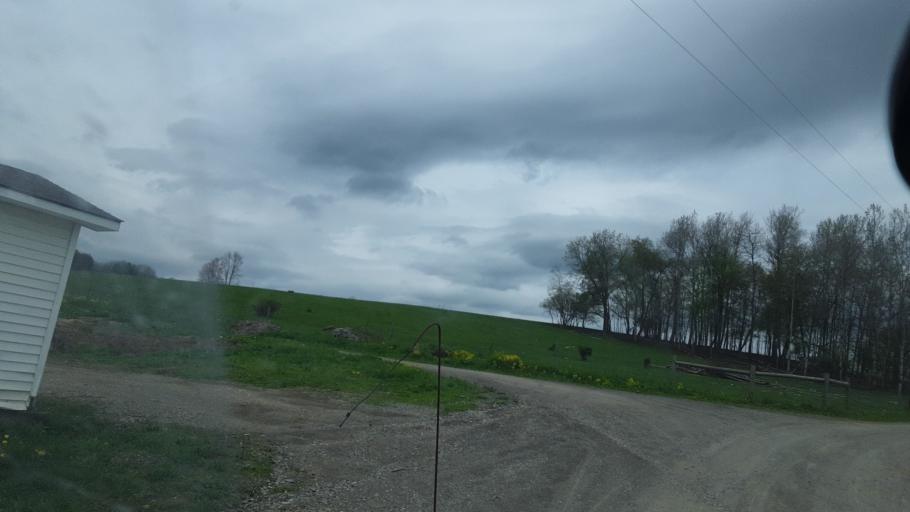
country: US
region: New York
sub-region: Steuben County
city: Addison
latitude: 42.0986
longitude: -77.2622
